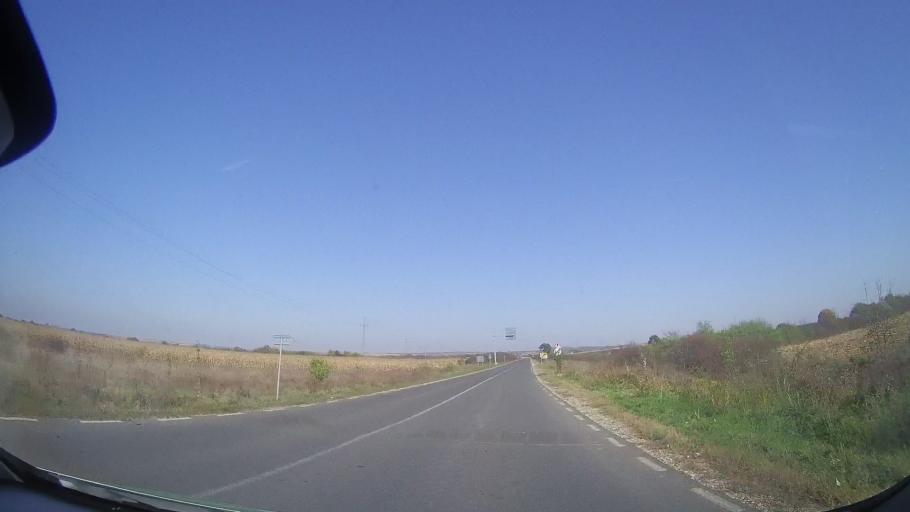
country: RO
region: Timis
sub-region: Comuna Balint
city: Balint
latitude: 45.7802
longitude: 21.8471
